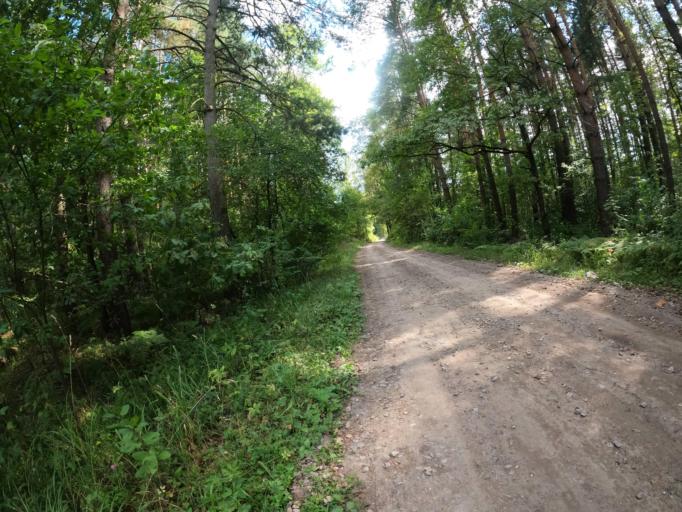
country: RU
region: Moskovskaya
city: Lopatinskiy
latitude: 55.3827
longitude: 38.7073
